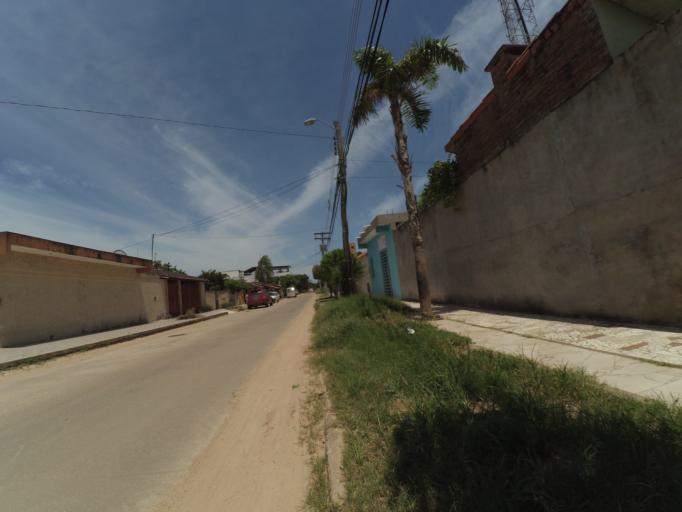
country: BO
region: Santa Cruz
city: Santa Cruz de la Sierra
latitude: -17.8135
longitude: -63.2238
